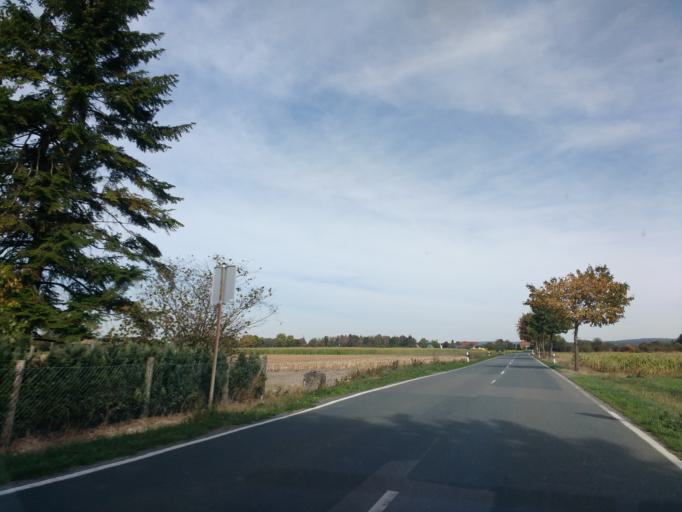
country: DE
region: North Rhine-Westphalia
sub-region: Regierungsbezirk Detmold
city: Schlangen
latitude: 51.7991
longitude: 8.8497
